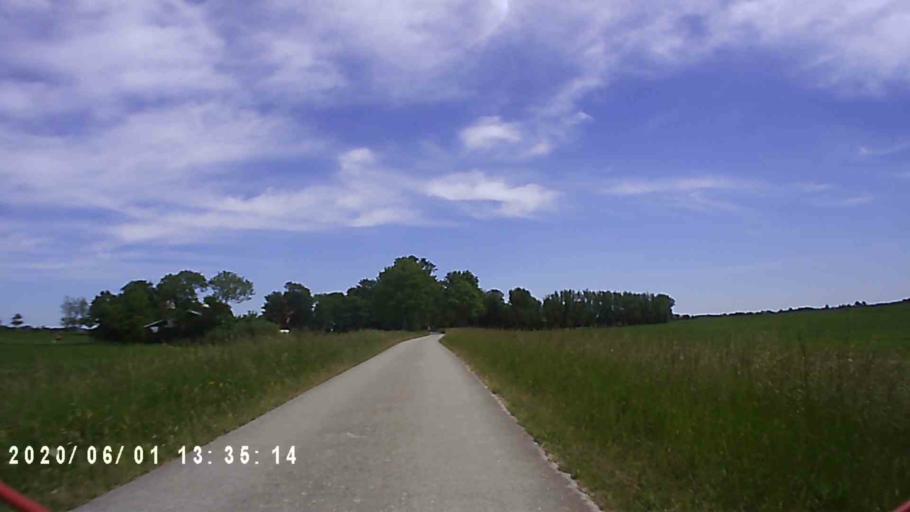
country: NL
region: Friesland
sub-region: Gemeente Littenseradiel
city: Wommels
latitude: 53.0878
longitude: 5.5798
